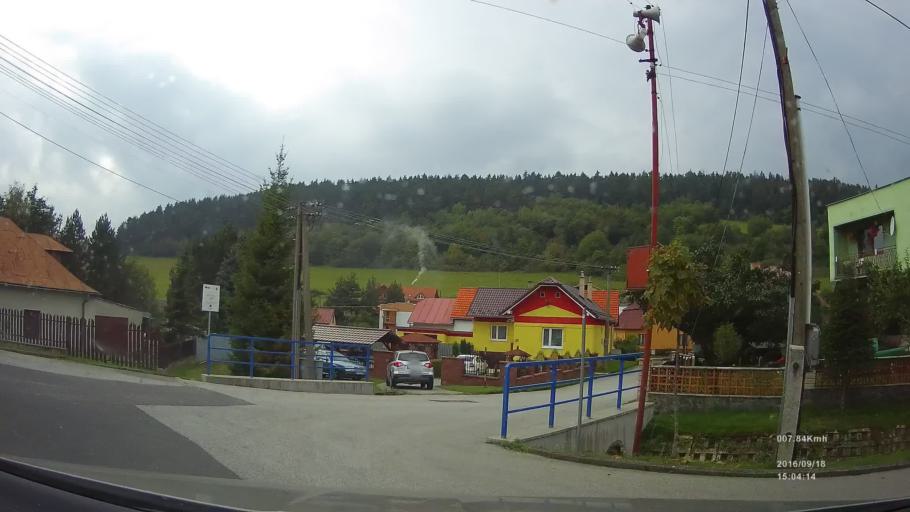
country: SK
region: Presovsky
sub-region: Okres Presov
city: Levoca
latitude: 49.0260
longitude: 20.5211
